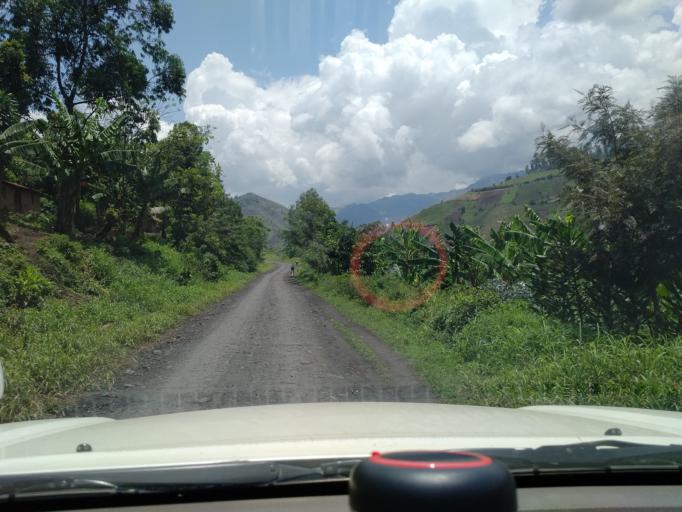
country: CD
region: Nord Kivu
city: Sake
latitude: -1.7392
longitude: 29.0014
